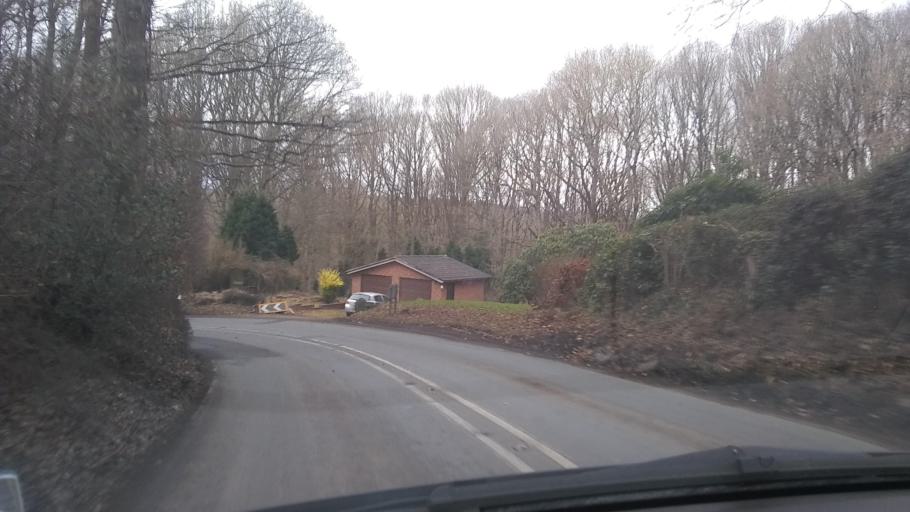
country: GB
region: England
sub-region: Shropshire
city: Cleobury Mortimer
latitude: 52.3769
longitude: -2.4354
